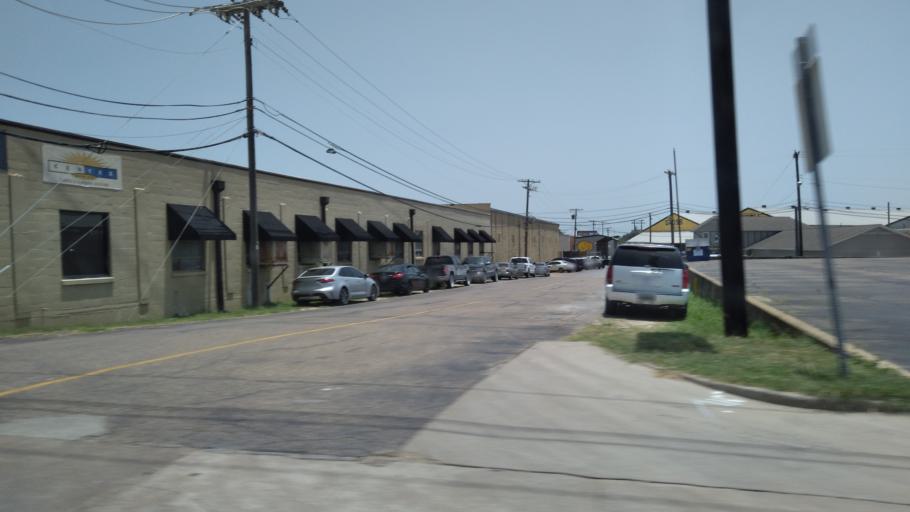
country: US
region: Texas
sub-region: McLennan County
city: Beverly Hills
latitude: 31.5296
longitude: -97.1607
